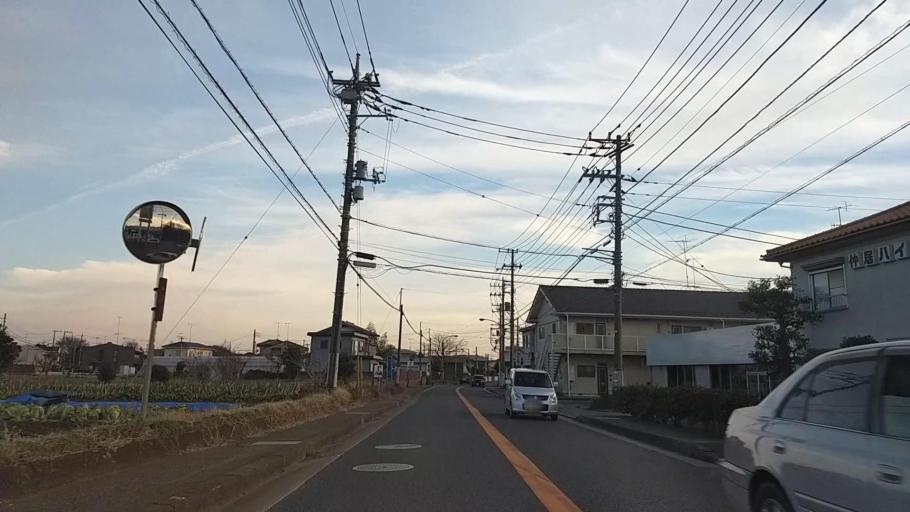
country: JP
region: Kanagawa
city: Atsugi
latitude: 35.4823
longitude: 139.3348
